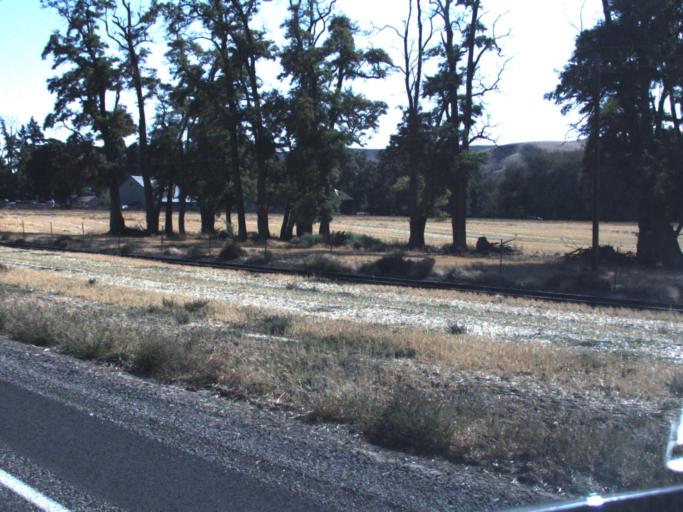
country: US
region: Washington
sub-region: Walla Walla County
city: Waitsburg
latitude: 46.2873
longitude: -118.2500
